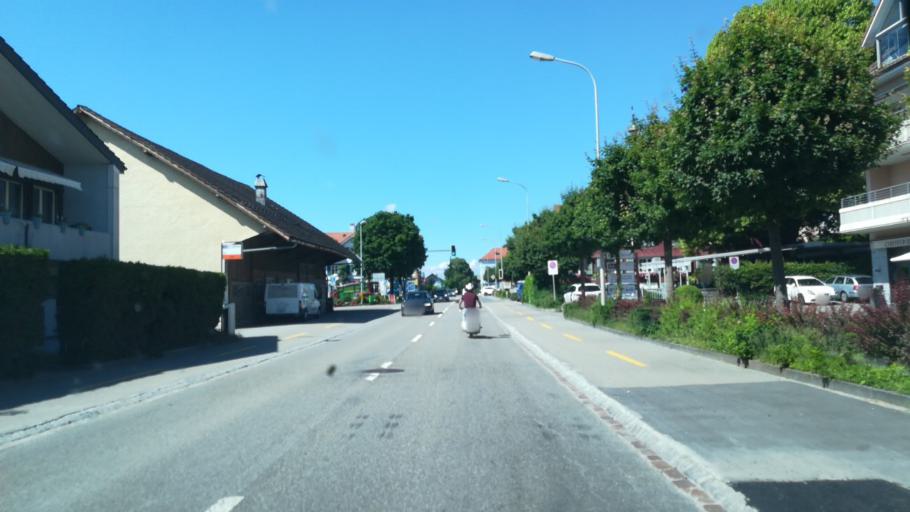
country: CH
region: Saint Gallen
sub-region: Wahlkreis St. Gallen
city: Andwil
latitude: 47.4421
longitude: 9.2553
